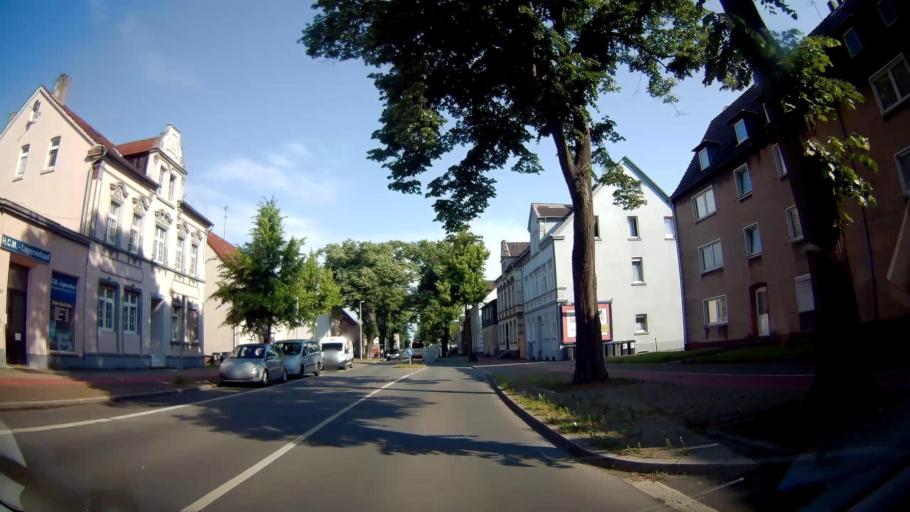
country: DE
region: North Rhine-Westphalia
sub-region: Regierungsbezirk Arnsberg
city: Herne
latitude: 51.5552
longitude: 7.2119
